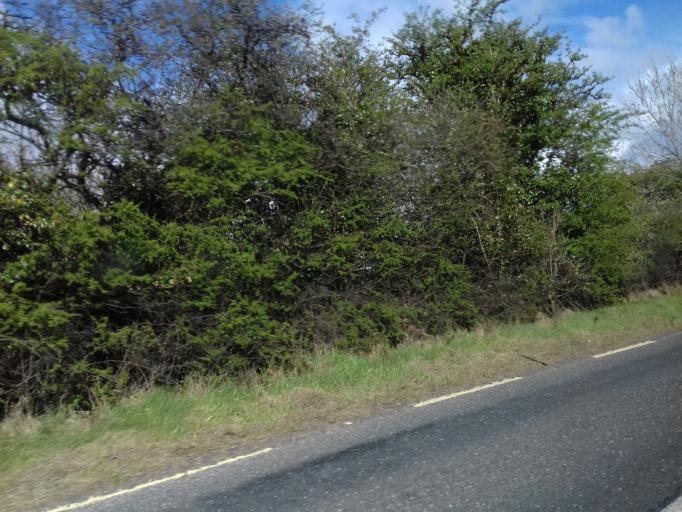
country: IE
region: Ulster
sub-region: County Donegal
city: Ballyshannon
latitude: 54.4915
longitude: -8.1527
